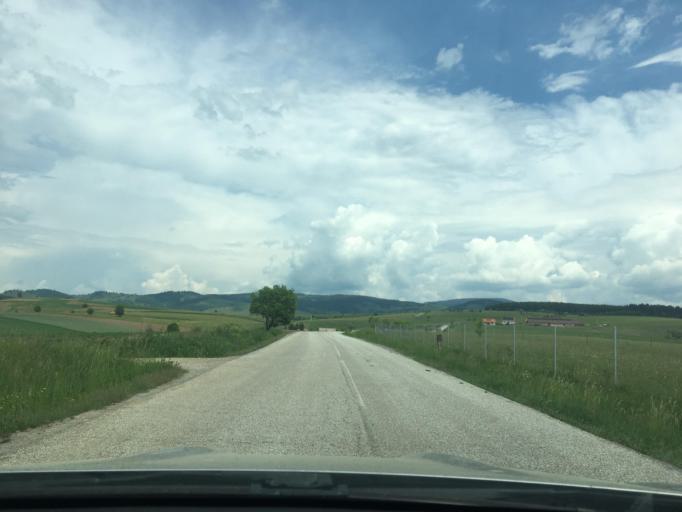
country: RO
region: Harghita
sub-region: Comuna Ditrau
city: Ditrau
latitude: 46.8402
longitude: 25.4970
